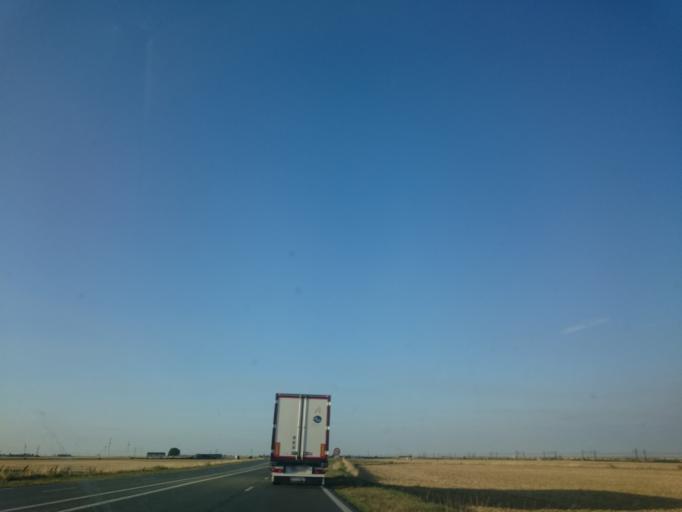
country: FR
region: Centre
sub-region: Departement du Loiret
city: Artenay
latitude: 48.1026
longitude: 1.8880
